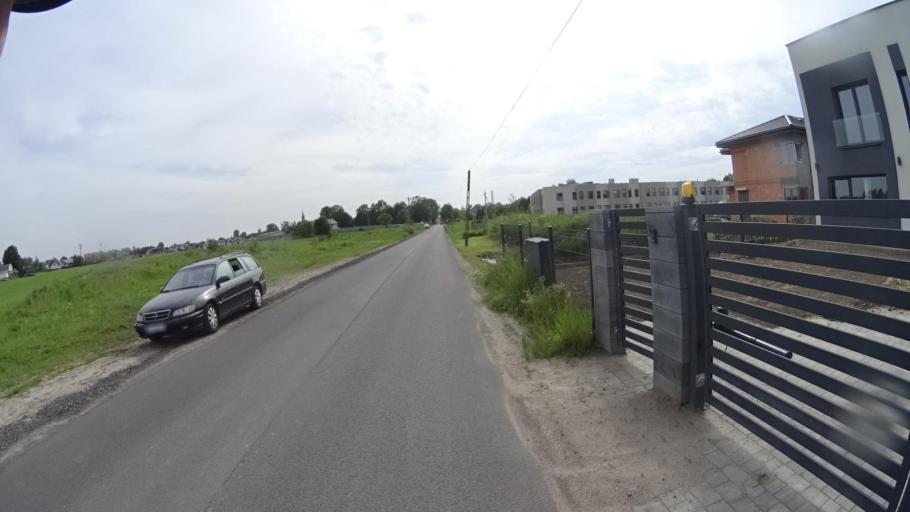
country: PL
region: Masovian Voivodeship
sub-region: Powiat pruszkowski
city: Pruszkow
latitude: 52.1876
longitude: 20.7974
